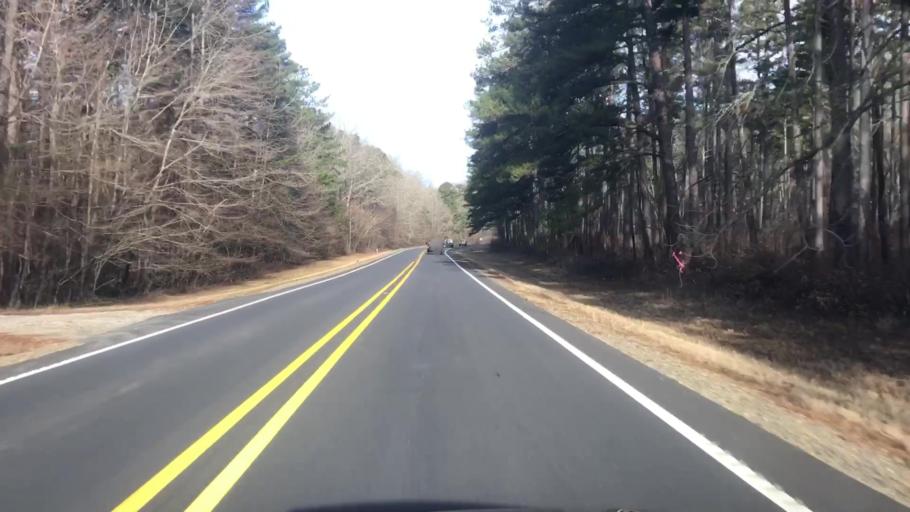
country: US
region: Arkansas
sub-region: Montgomery County
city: Mount Ida
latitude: 34.5182
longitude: -93.3868
